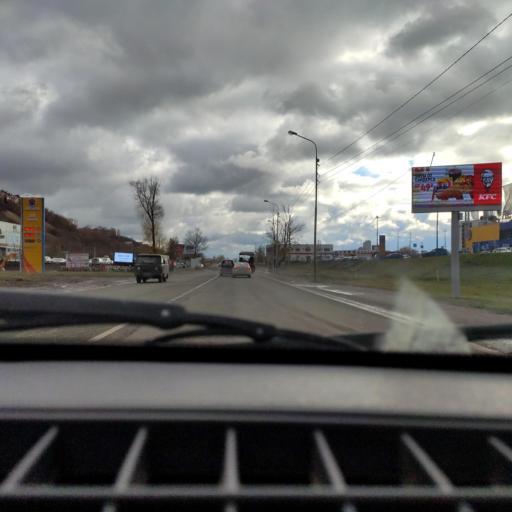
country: RU
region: Bashkortostan
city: Ufa
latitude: 54.6977
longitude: 55.9717
